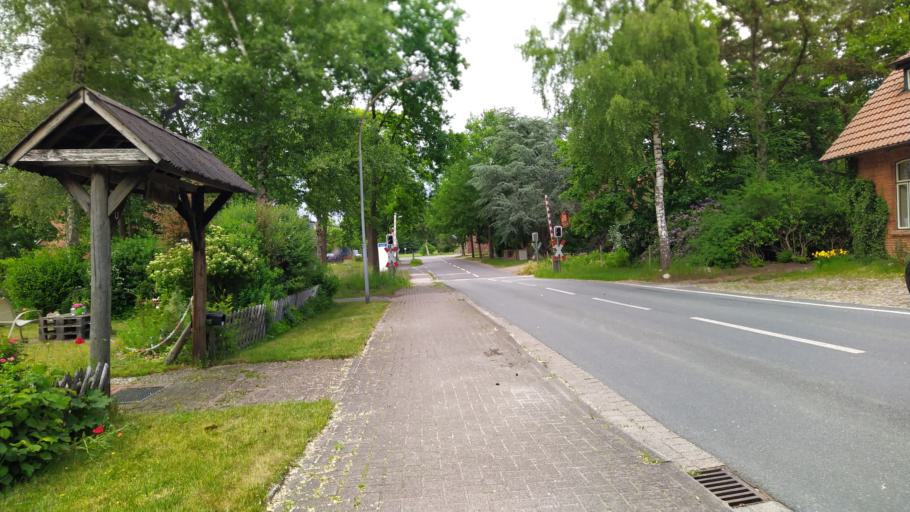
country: DE
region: Lower Saxony
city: Brest
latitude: 53.4600
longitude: 9.3836
